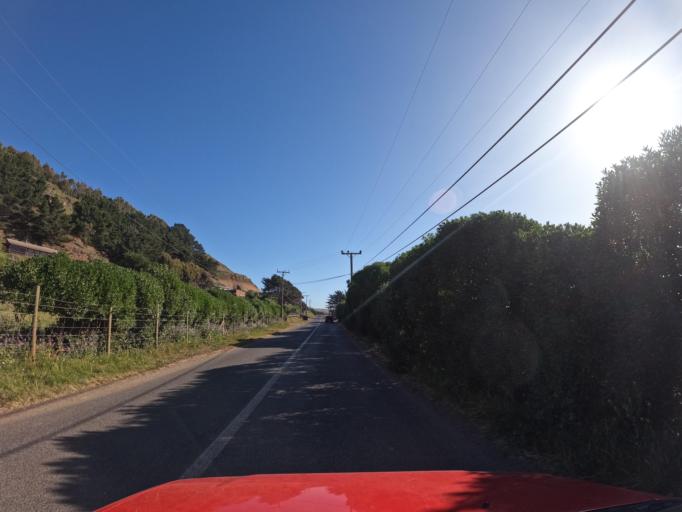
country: CL
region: Maule
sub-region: Provincia de Talca
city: Constitucion
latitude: -34.8689
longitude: -72.1496
